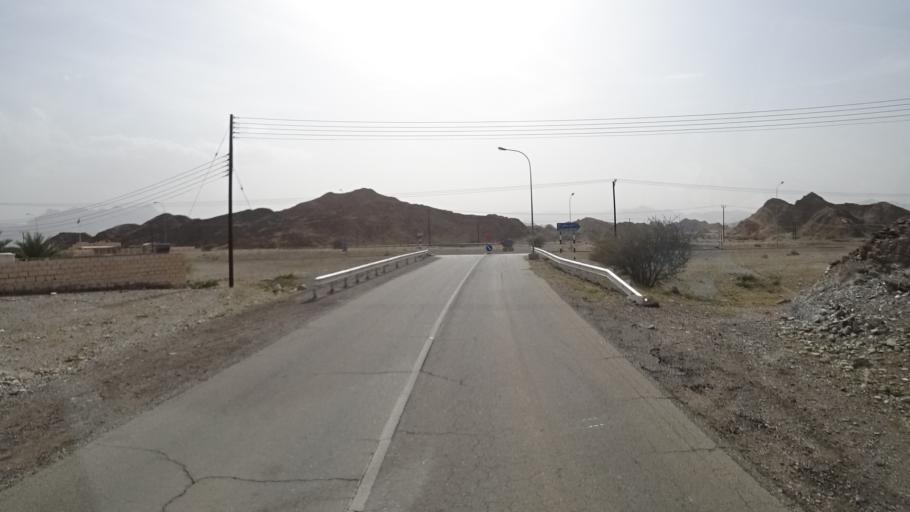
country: OM
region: Muhafazat Masqat
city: Bawshar
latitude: 23.3868
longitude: 58.5132
